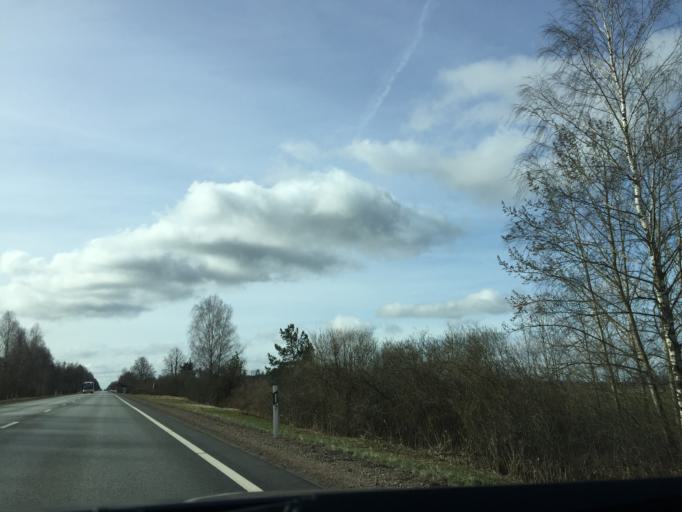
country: LV
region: Jelgava
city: Jelgava
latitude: 56.5746
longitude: 23.7145
